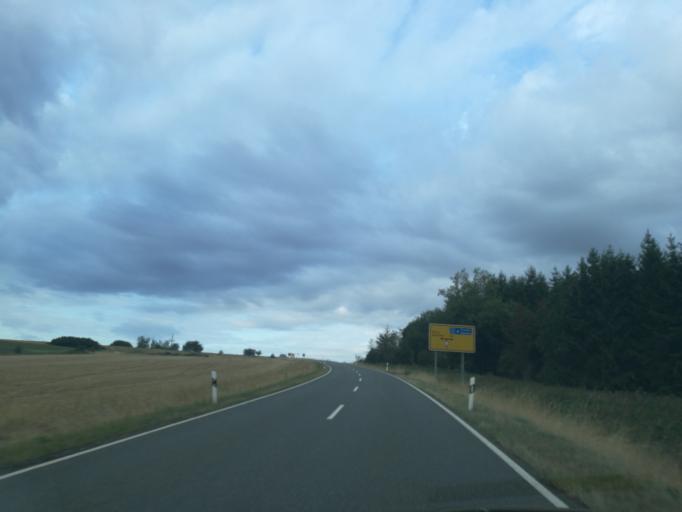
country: DE
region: Bavaria
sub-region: Upper Franconia
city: Regnitzlosau
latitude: 50.3105
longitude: 12.0309
